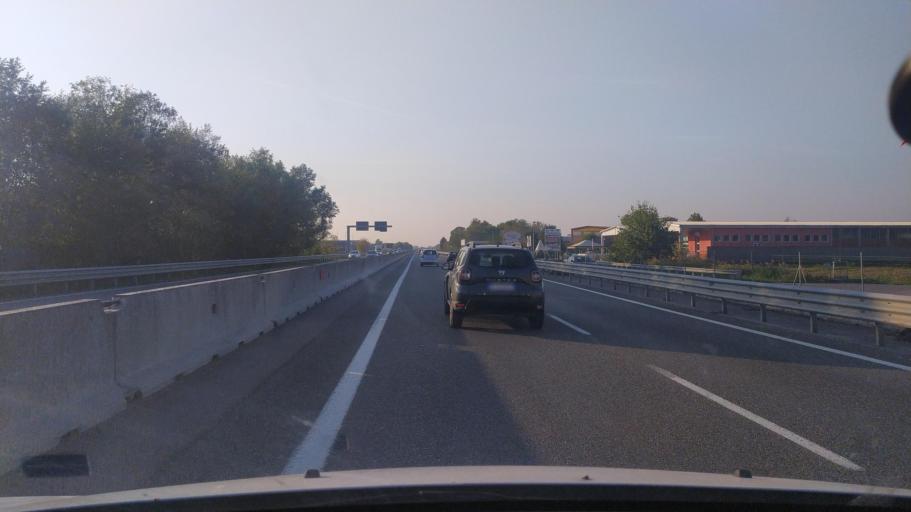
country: IT
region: Lombardy
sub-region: Provincia di Cremona
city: Bagnolo Cremasco
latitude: 45.3672
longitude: 9.6248
